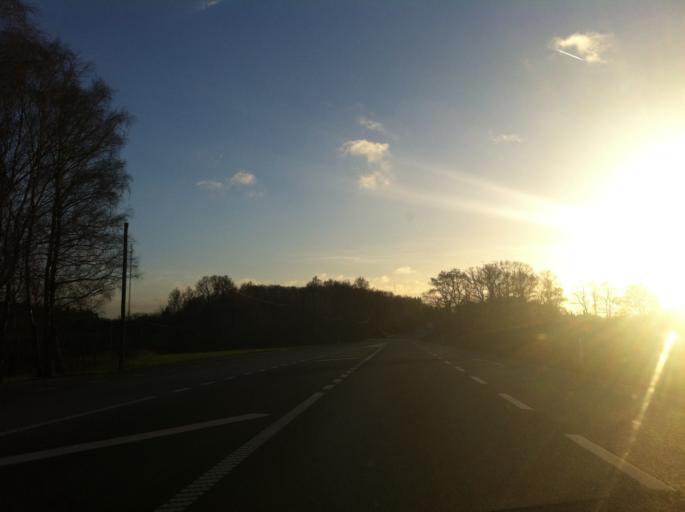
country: SE
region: Skane
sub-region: Hassleholms Kommun
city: Hassleholm
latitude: 56.1267
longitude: 13.7989
